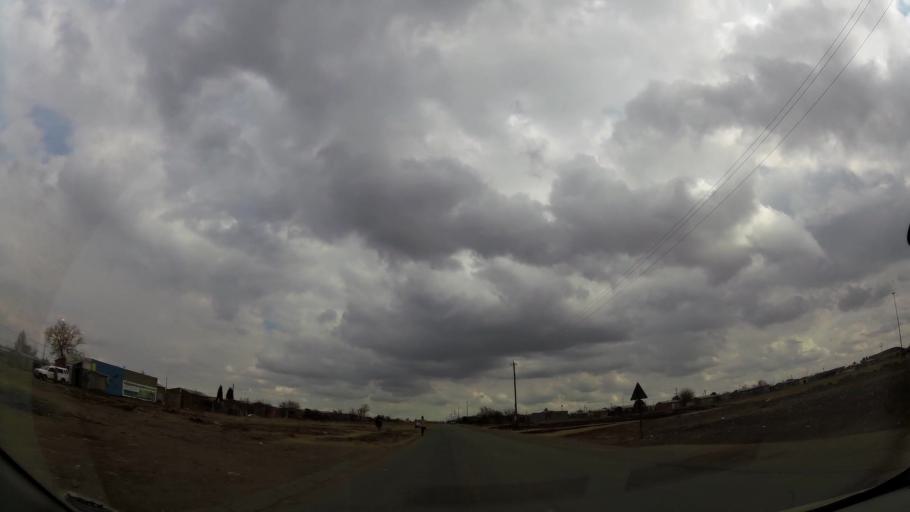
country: ZA
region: Orange Free State
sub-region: Fezile Dabi District Municipality
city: Sasolburg
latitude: -26.8501
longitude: 27.8747
